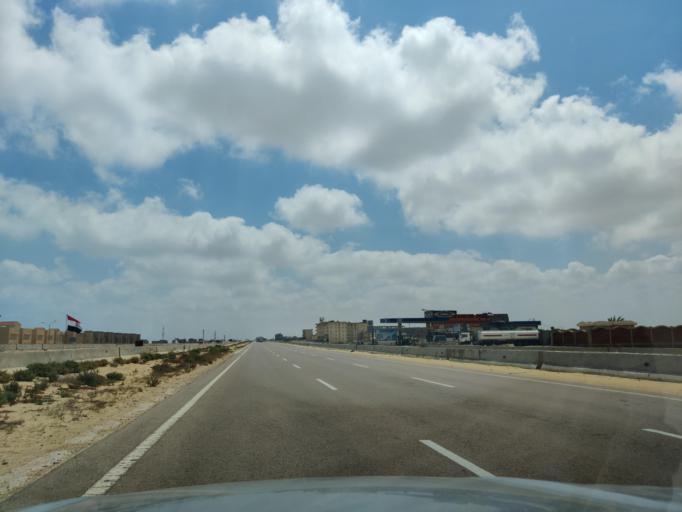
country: EG
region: Muhafazat Matruh
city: Al `Alamayn
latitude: 30.8187
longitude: 29.1558
